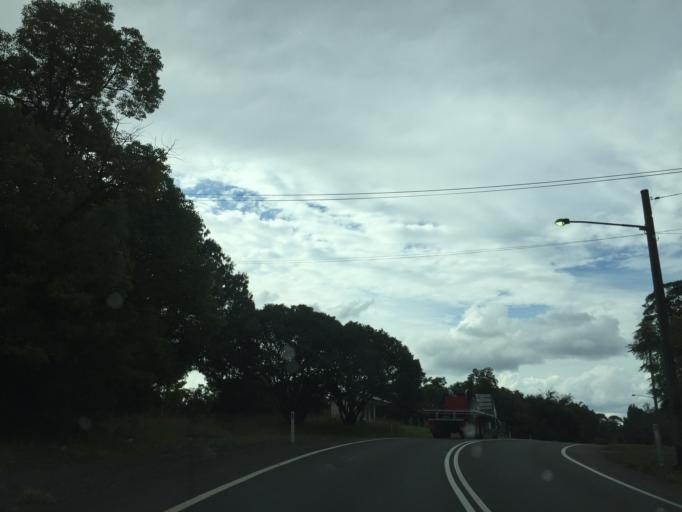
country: AU
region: New South Wales
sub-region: Hornsby Shire
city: Galston
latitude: -33.6547
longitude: 151.0398
